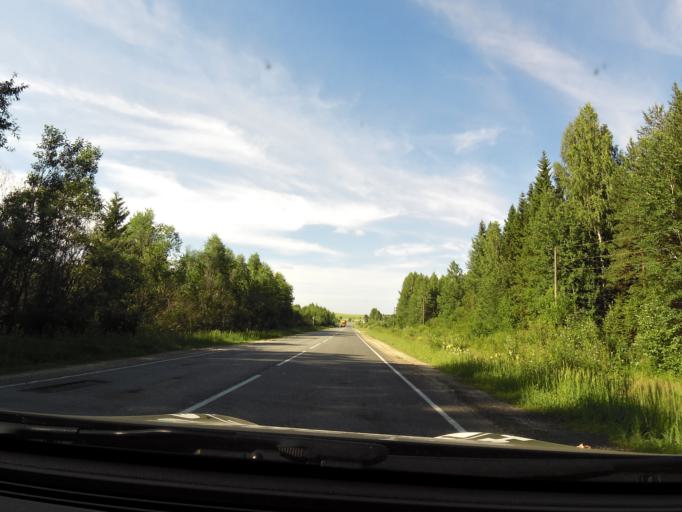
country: RU
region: Kirov
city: Belaya Kholunitsa
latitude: 58.8853
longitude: 50.8737
